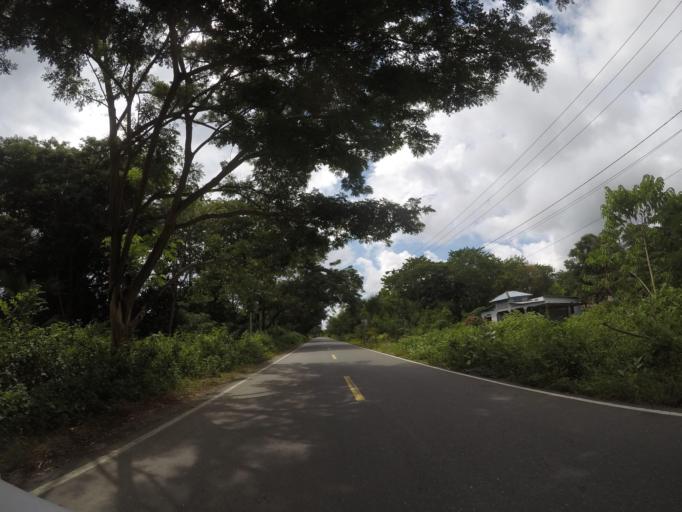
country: TL
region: Liquica
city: Maubara
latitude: -8.7305
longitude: 125.1296
